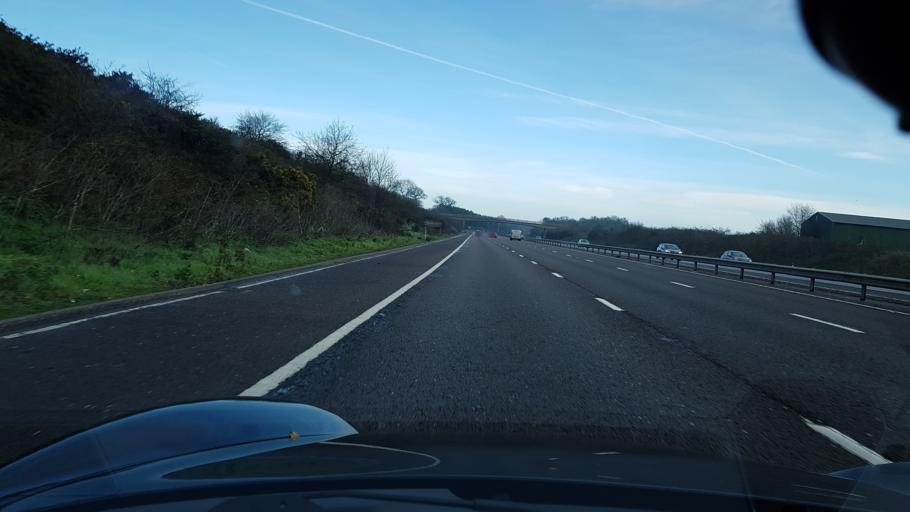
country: GB
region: England
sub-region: Surrey
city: Cobham
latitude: 51.3400
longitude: -0.4101
